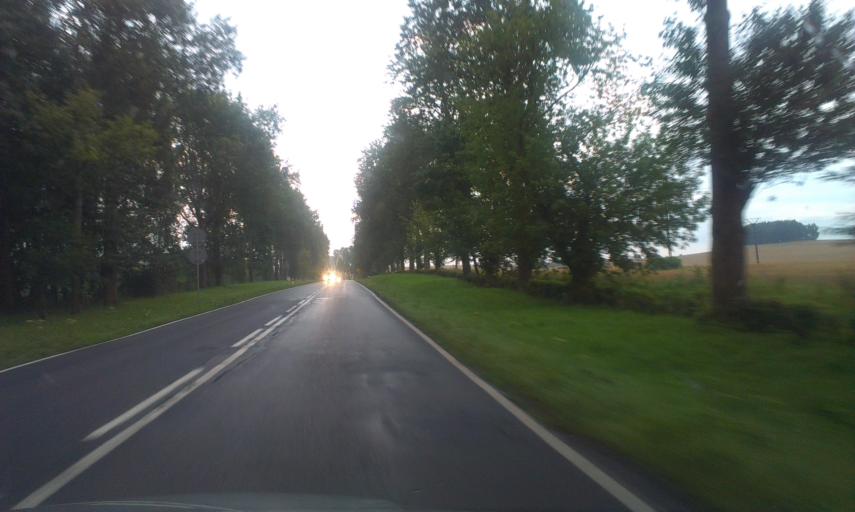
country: PL
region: West Pomeranian Voivodeship
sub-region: Koszalin
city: Koszalin
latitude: 54.1486
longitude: 16.2455
